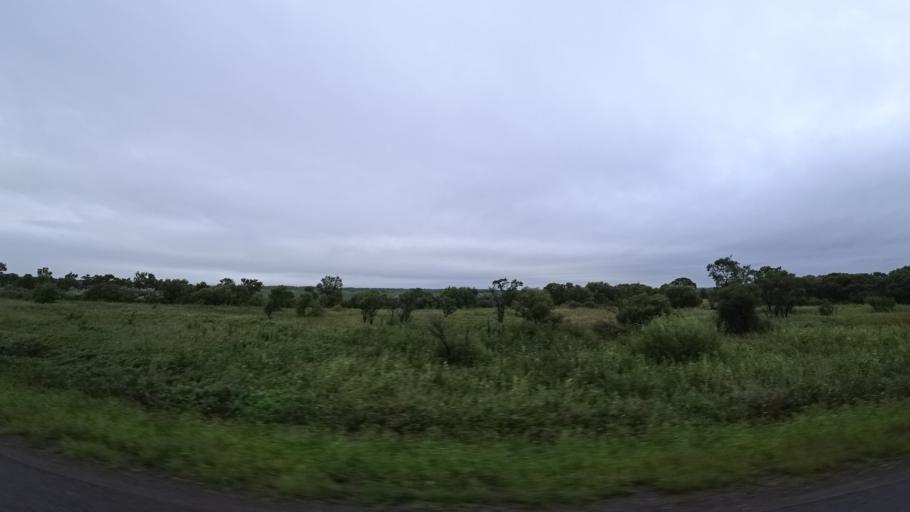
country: RU
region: Primorskiy
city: Chernigovka
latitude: 44.2927
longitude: 132.5121
